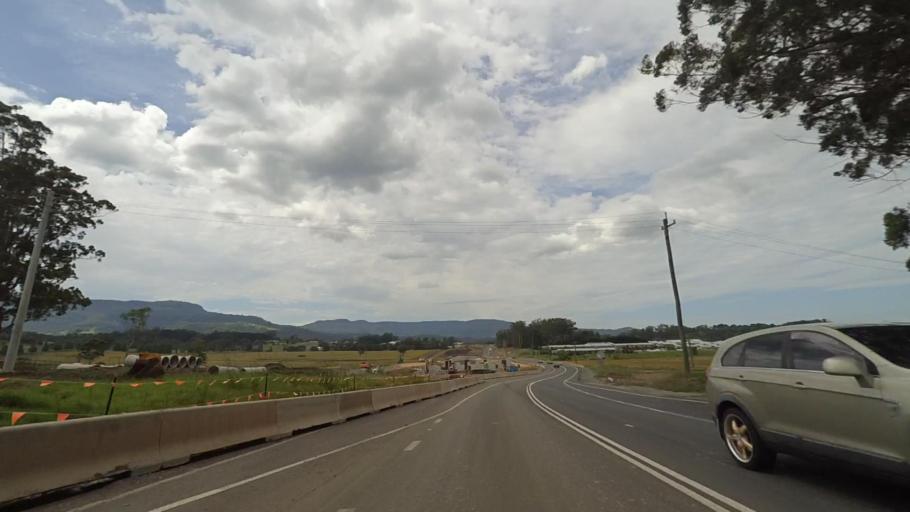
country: AU
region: New South Wales
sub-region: Shoalhaven Shire
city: Berry
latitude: -34.7822
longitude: 150.6789
